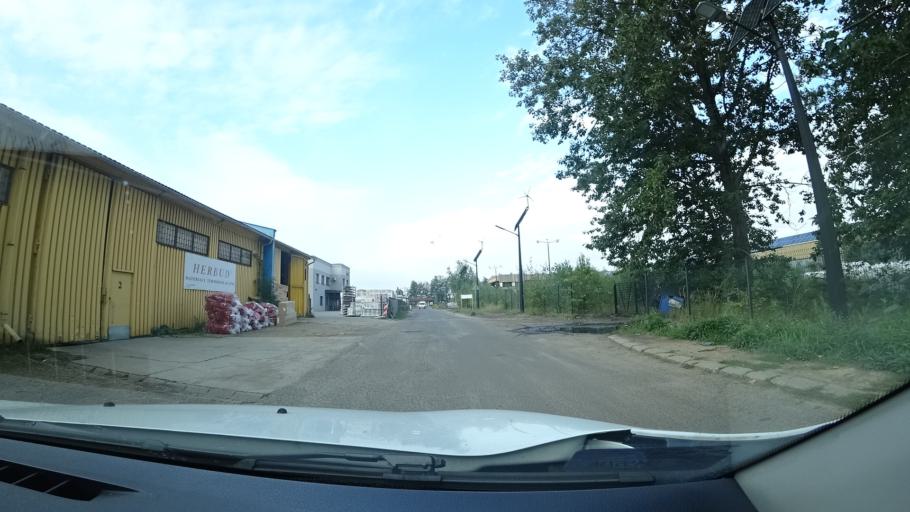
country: PL
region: Silesian Voivodeship
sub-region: Siemianowice Slaskie
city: Siemianowice Slaskie
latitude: 50.3286
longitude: 19.0132
